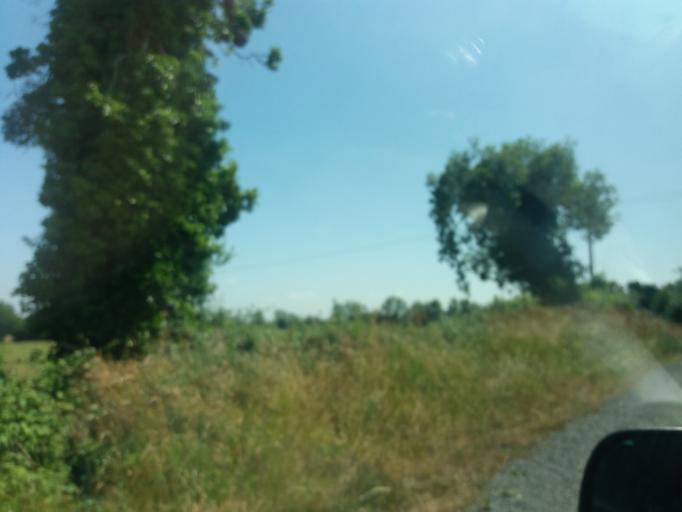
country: IE
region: Leinster
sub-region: An Mhi
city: Ashbourne
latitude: 53.5263
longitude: -6.3022
